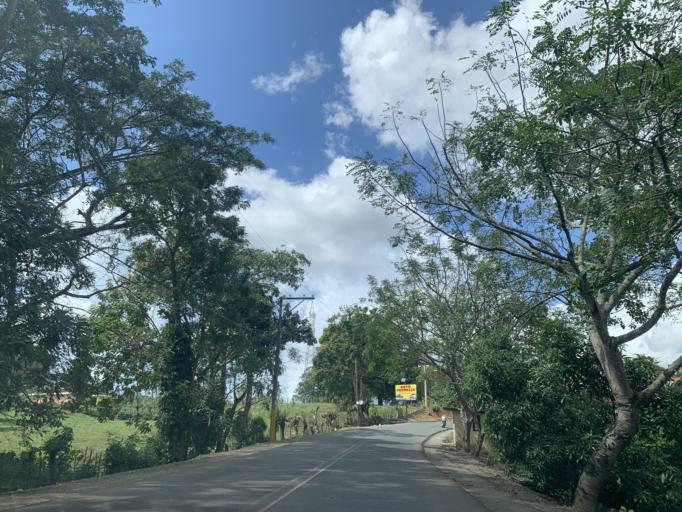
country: DO
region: Monte Plata
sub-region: Yamasa
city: Yamasa
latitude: 18.7607
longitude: -70.0187
